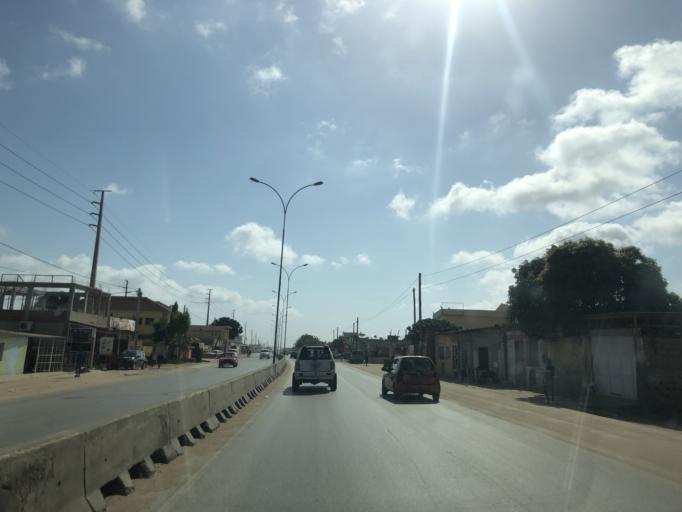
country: AO
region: Luanda
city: Luanda
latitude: -8.9026
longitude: 13.2497
